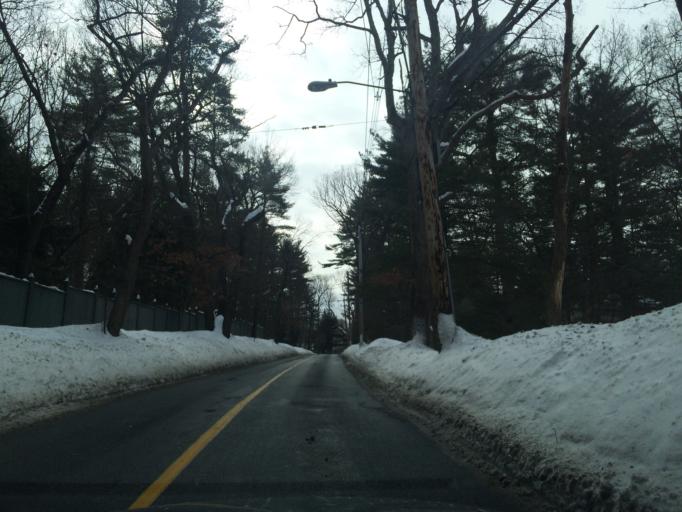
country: US
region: Massachusetts
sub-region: Middlesex County
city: Weston
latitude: 42.3490
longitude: -71.2822
